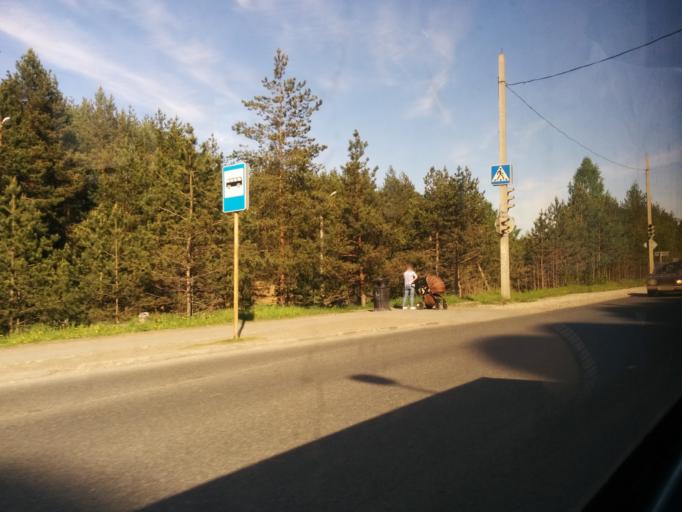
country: RU
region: Perm
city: Kondratovo
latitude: 58.0374
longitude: 56.1391
